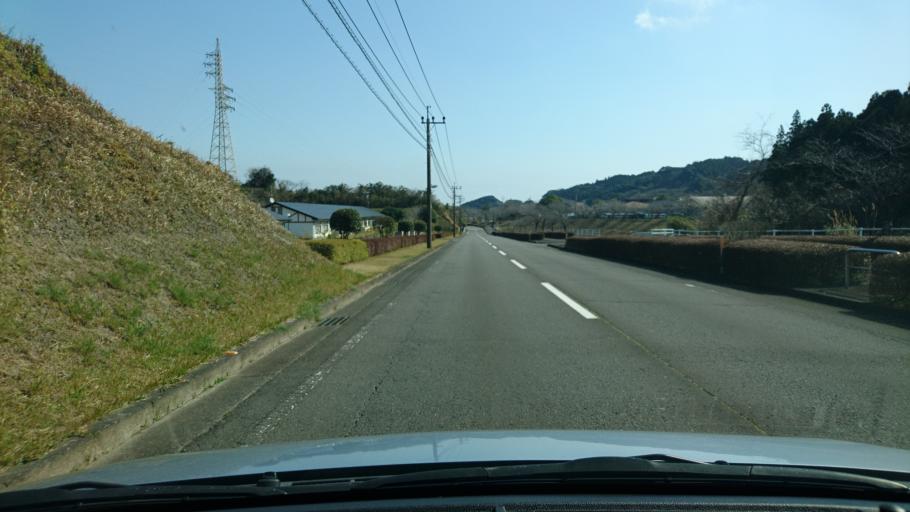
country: JP
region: Miyazaki
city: Miyazaki-shi
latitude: 31.8362
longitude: 131.3941
